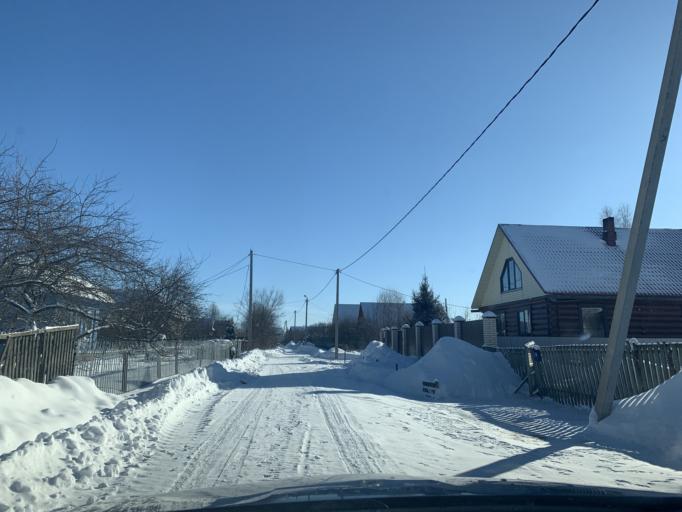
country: RU
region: Jaroslavl
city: Tunoshna
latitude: 57.6524
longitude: 40.0615
